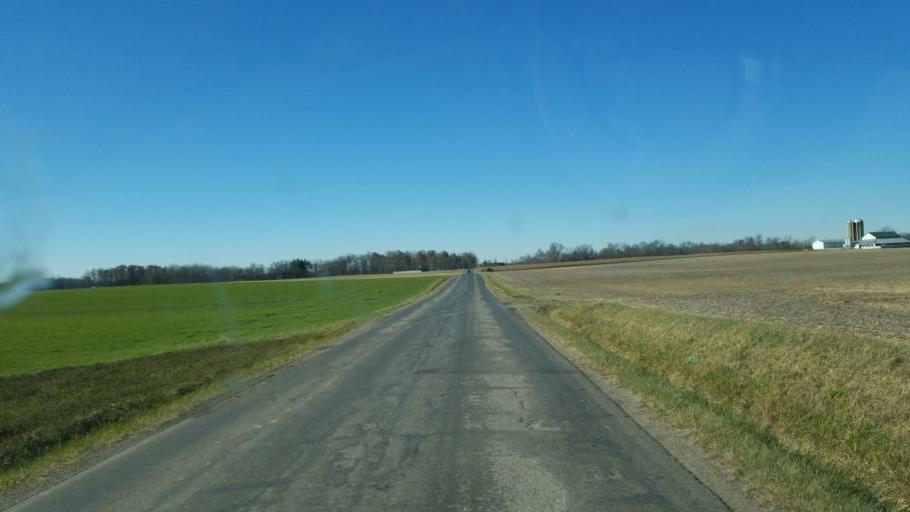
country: US
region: Ohio
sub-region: Huron County
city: Greenwich
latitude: 40.9603
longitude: -82.5622
